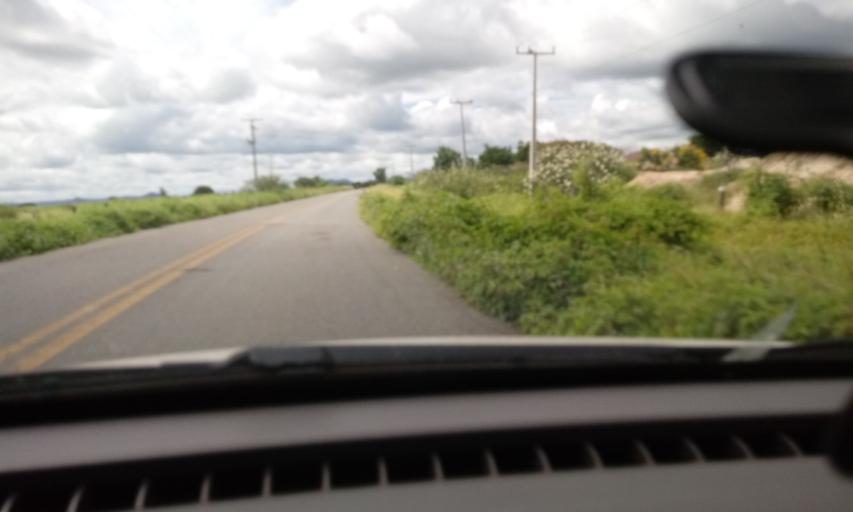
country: BR
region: Bahia
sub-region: Guanambi
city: Guanambi
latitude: -13.9617
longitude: -42.8554
